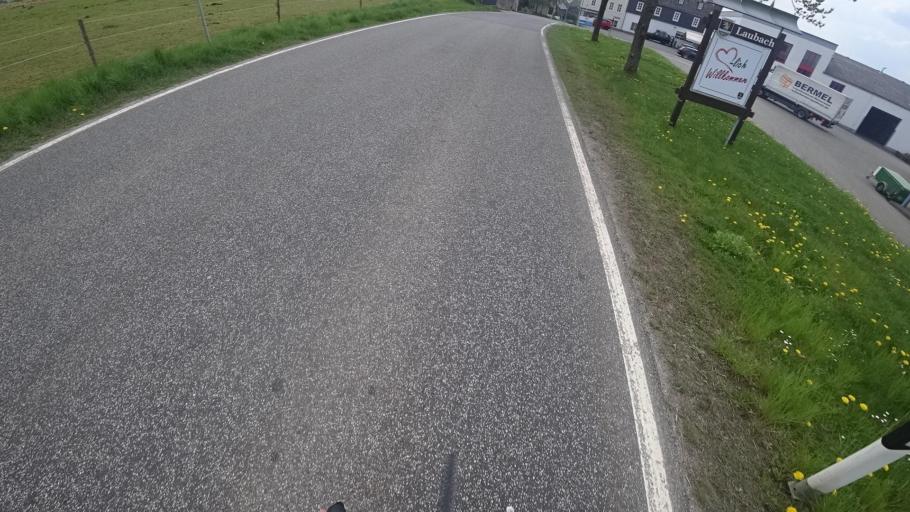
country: DE
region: Rheinland-Pfalz
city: Laubach
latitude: 50.0563
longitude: 7.5133
